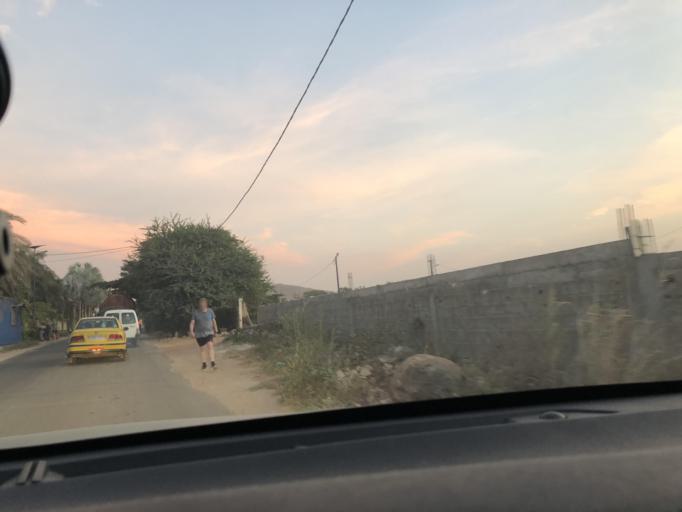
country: SN
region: Dakar
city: Mermoz Boabab
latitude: 14.7352
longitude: -17.5115
